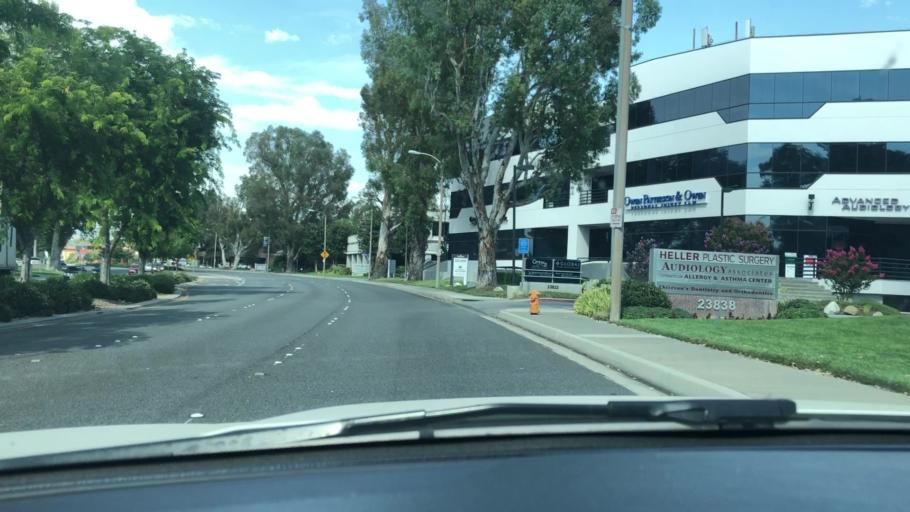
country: US
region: California
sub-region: Los Angeles County
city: Santa Clarita
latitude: 34.4134
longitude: -118.5521
